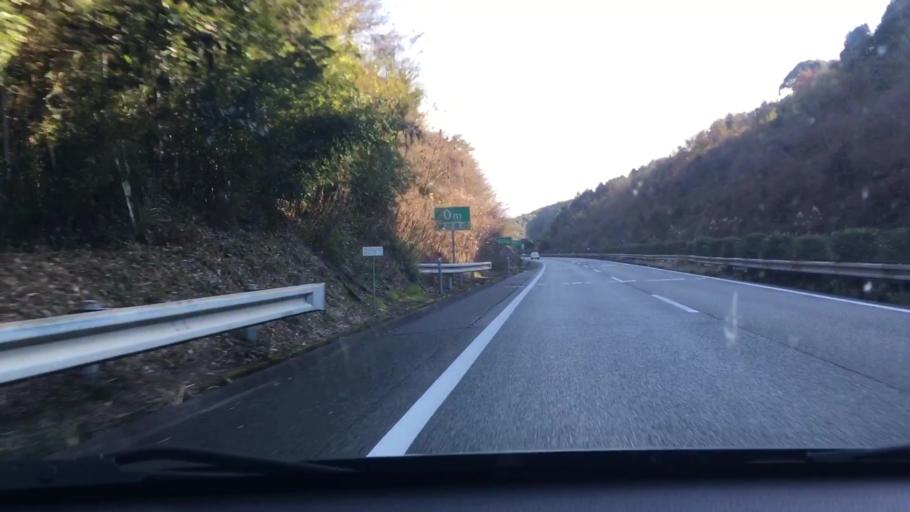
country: JP
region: Kumamoto
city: Hitoyoshi
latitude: 32.1741
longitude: 130.7900
